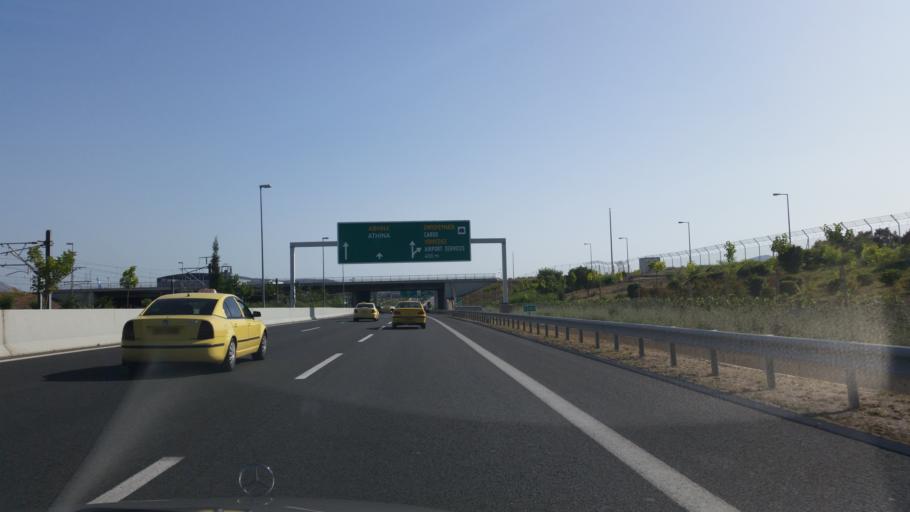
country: GR
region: Attica
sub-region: Nomarchia Anatolikis Attikis
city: Spata
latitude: 37.9331
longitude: 23.9406
